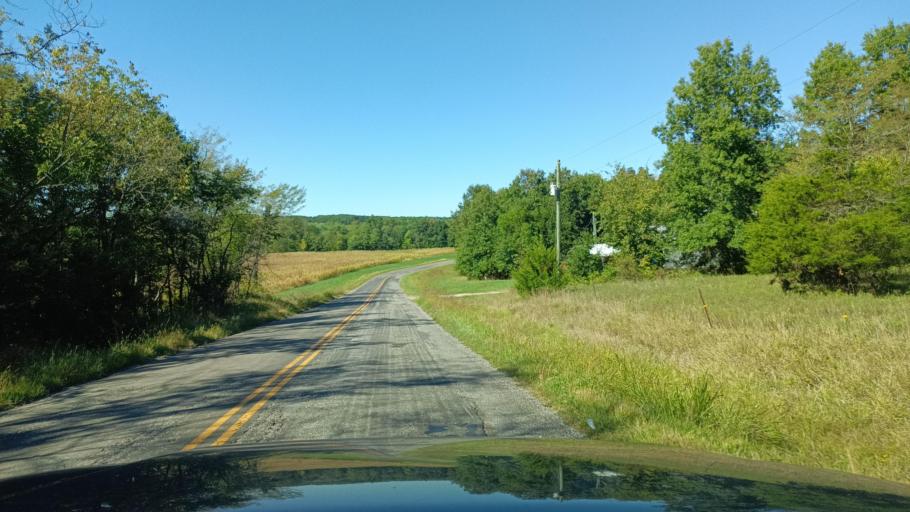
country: US
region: Missouri
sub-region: Scotland County
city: Memphis
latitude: 40.3522
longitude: -92.2410
